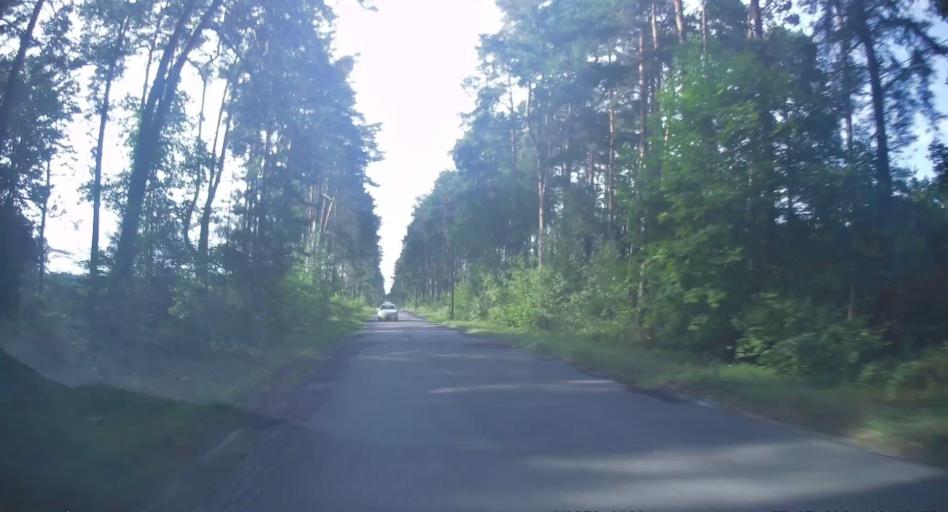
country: PL
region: Swietokrzyskie
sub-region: Powiat konecki
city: Konskie
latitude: 51.2210
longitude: 20.3883
